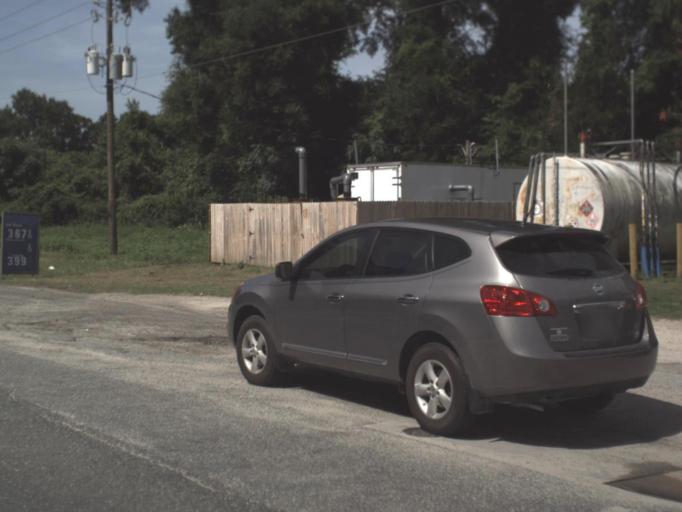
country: US
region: Florida
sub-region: Lafayette County
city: Mayo
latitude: 30.1220
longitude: -83.1697
